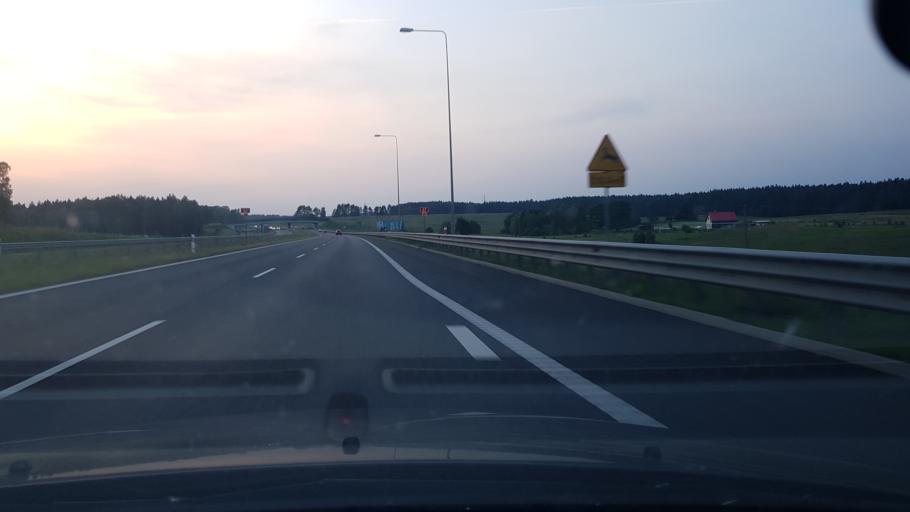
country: PL
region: Warmian-Masurian Voivodeship
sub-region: Powiat olsztynski
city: Olsztynek
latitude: 53.5055
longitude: 20.3089
